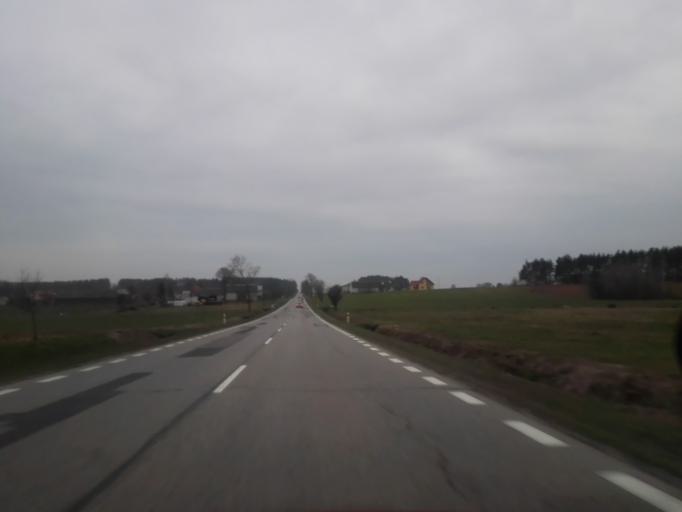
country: PL
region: Podlasie
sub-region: Powiat lomzynski
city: Piatnica
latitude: 53.2779
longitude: 22.1359
